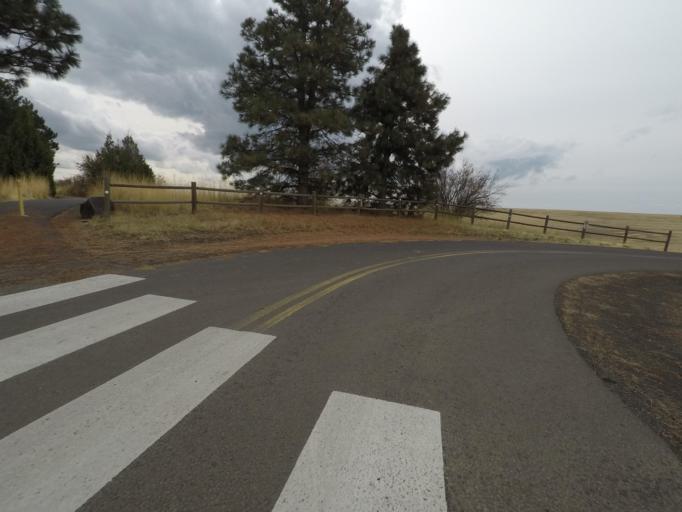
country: US
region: Washington
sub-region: Walla Walla County
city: Walla Walla East
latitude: 46.0661
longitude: -118.2673
